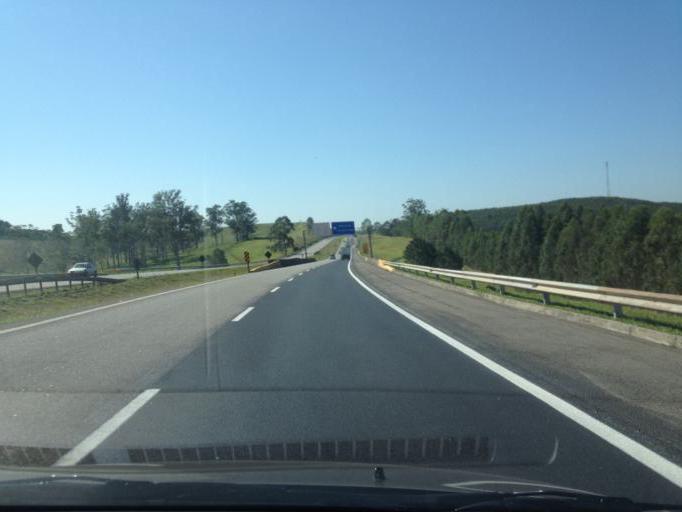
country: BR
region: Sao Paulo
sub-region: Guararema
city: Guararema
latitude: -23.3597
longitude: -46.1228
